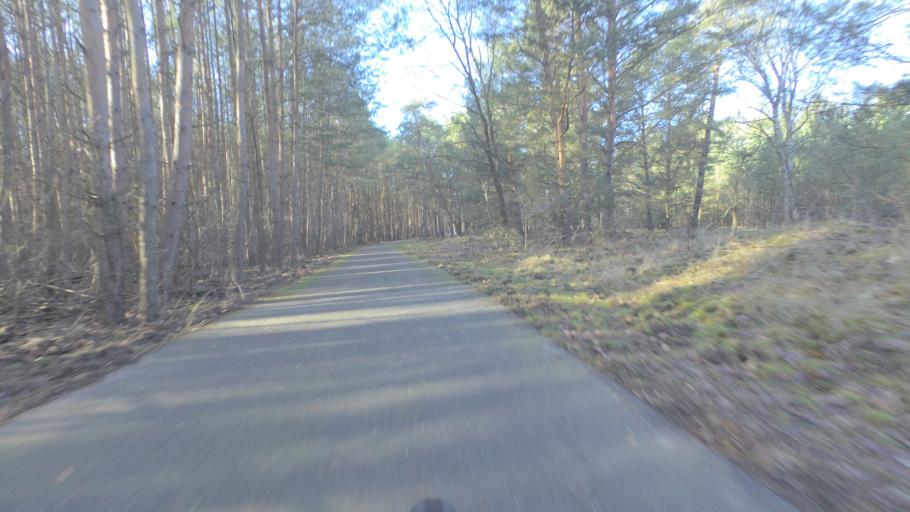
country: DE
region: Brandenburg
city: Luckenwalde
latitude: 52.0523
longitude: 13.1612
